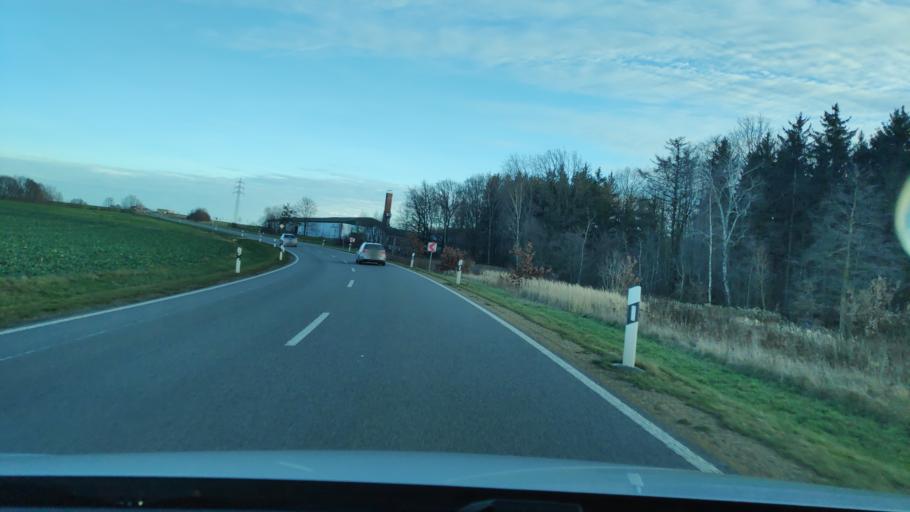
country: DE
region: Saxony
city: Mulsen
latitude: 50.7553
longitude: 12.5409
